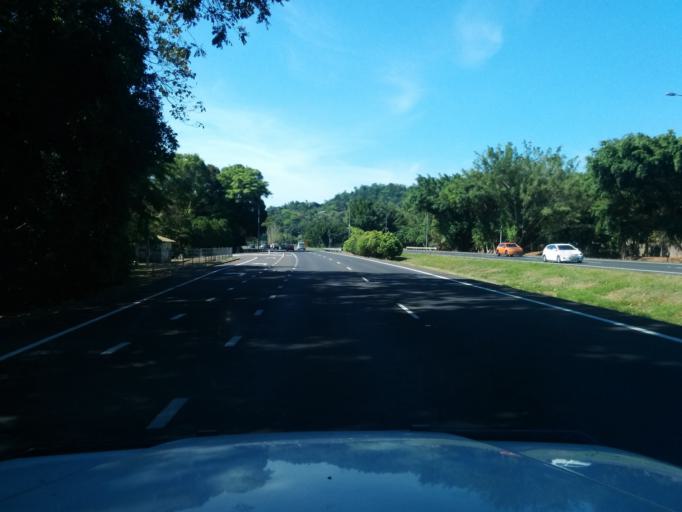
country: AU
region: Queensland
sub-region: Cairns
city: Redlynch
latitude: -16.9000
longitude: 145.7094
